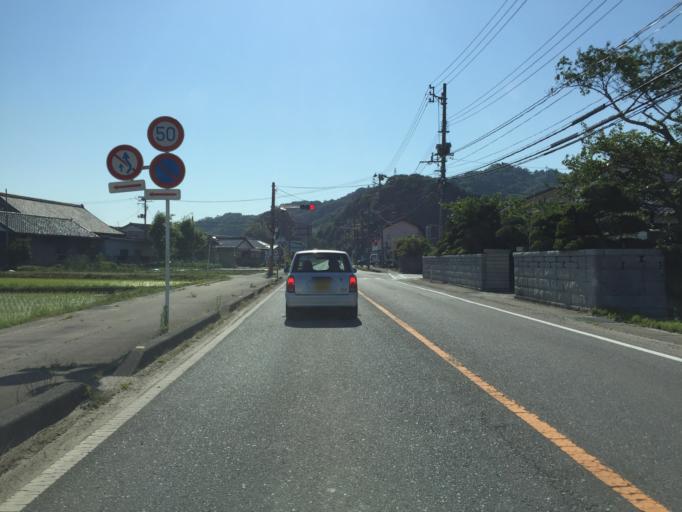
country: JP
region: Fukushima
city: Iwaki
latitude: 36.9596
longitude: 140.8340
